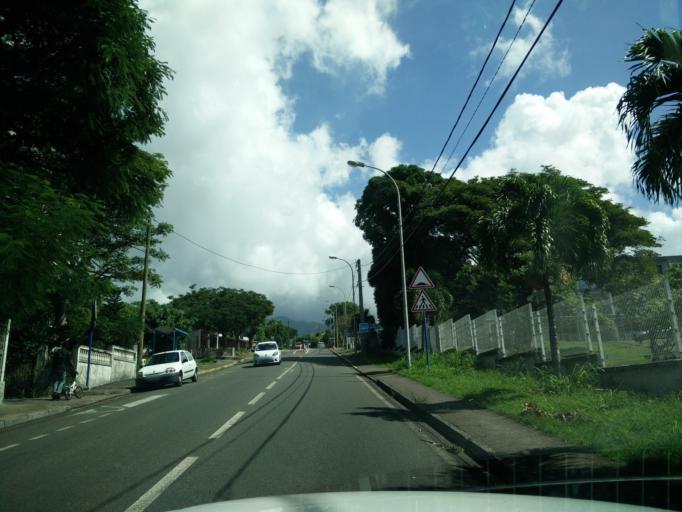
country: GP
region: Guadeloupe
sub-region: Guadeloupe
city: Basse-Terre
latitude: 15.9930
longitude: -61.7198
